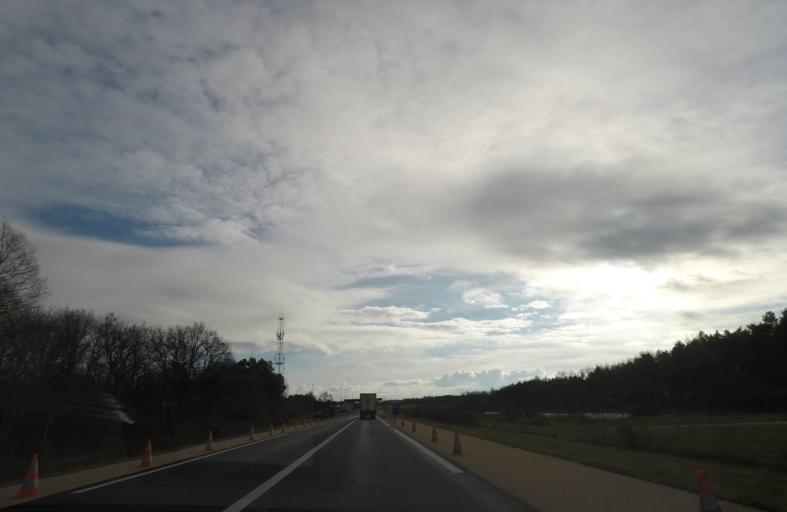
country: FR
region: Centre
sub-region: Departement du Loir-et-Cher
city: Villefranche-sur-Cher
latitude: 47.3264
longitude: 1.7631
